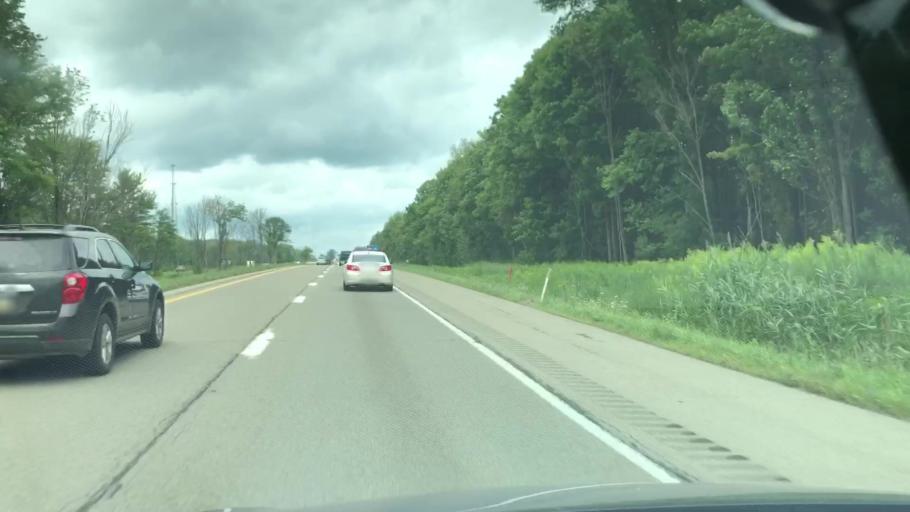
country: US
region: Pennsylvania
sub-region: Erie County
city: Edinboro
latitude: 41.8625
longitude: -80.1764
